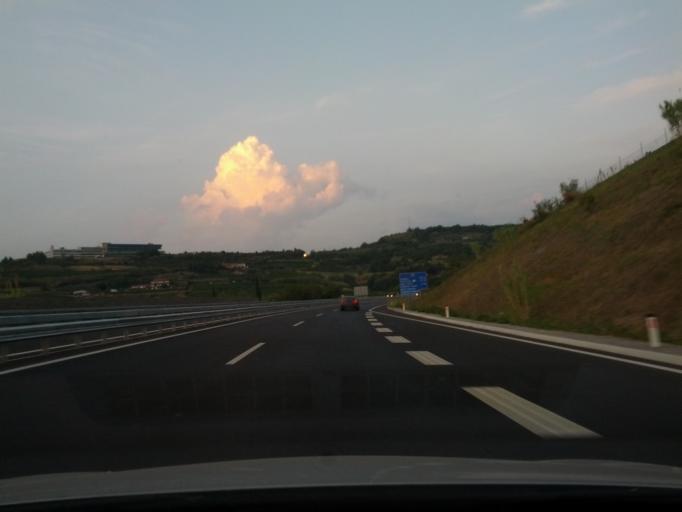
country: SI
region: Izola-Isola
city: Izola
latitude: 45.5375
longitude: 13.6788
